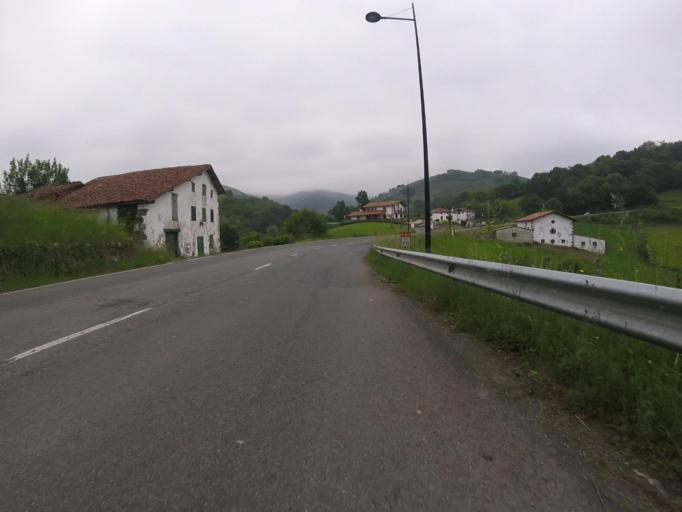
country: ES
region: Navarre
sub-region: Provincia de Navarra
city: Zugarramurdi
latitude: 43.2721
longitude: -1.4945
